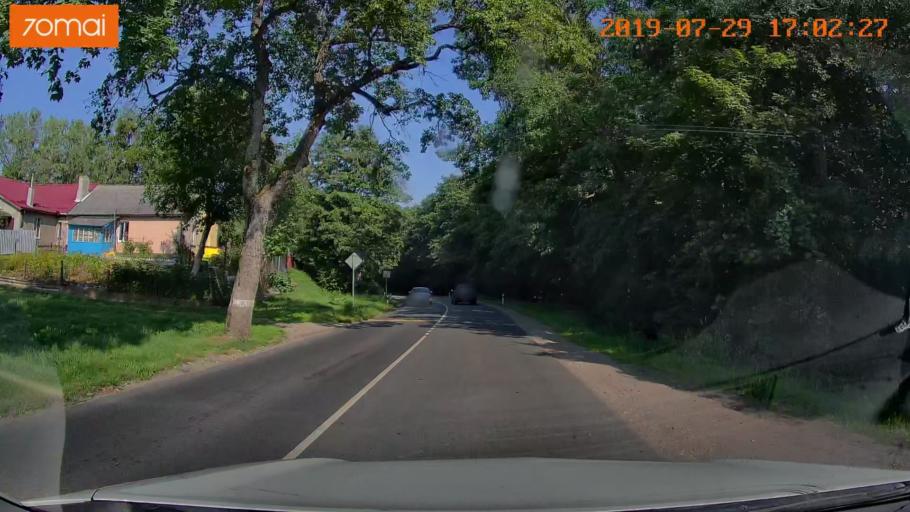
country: RU
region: Kaliningrad
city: Volochayevskoye
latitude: 54.8150
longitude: 20.2566
